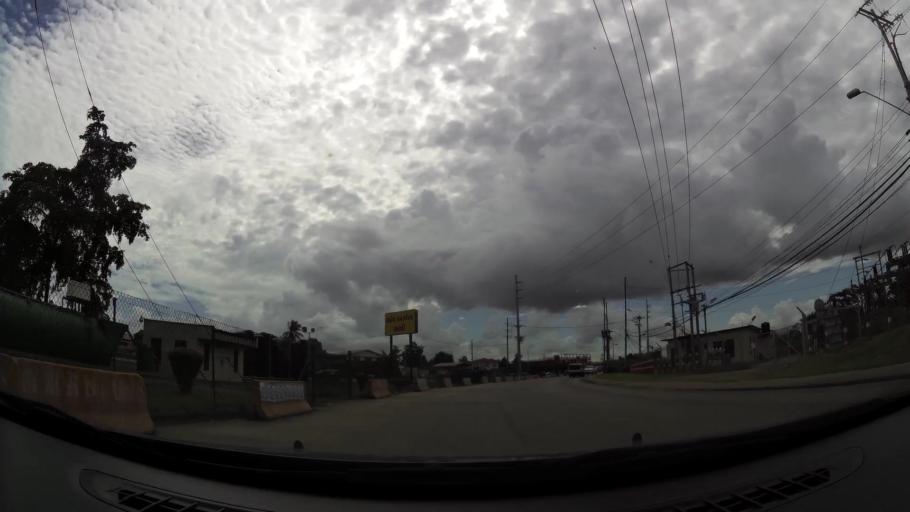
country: TT
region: Chaguanas
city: Chaguanas
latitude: 10.5110
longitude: -61.4081
